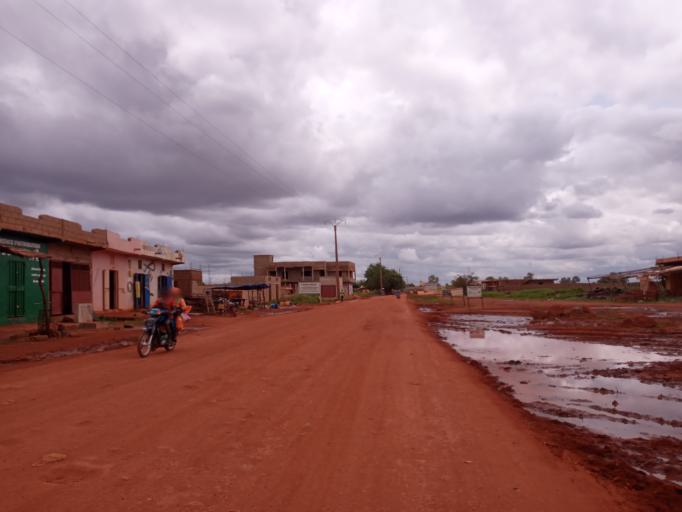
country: ML
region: Bamako
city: Bamako
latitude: 12.5409
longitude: -7.9943
